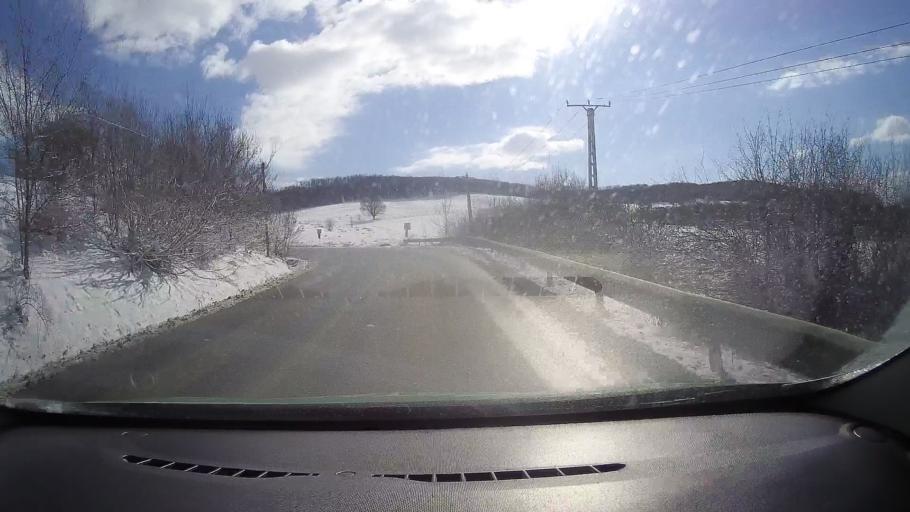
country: RO
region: Sibiu
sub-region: Comuna Barghis
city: Barghis
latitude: 45.9813
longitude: 24.5105
